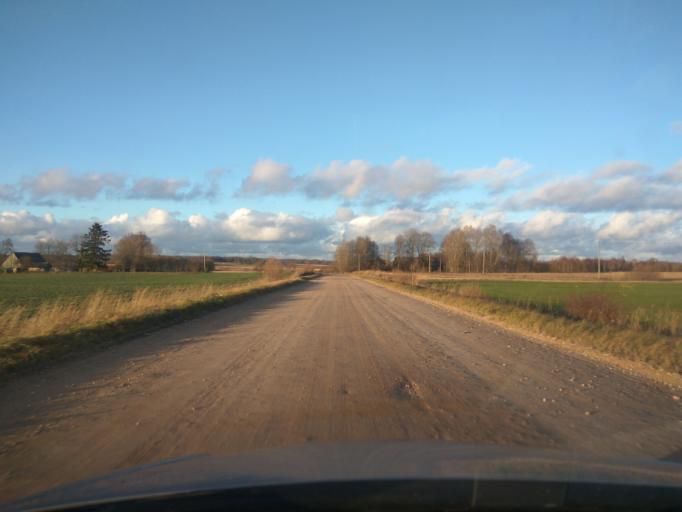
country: LV
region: Aizpute
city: Aizpute
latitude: 56.8051
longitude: 21.7871
